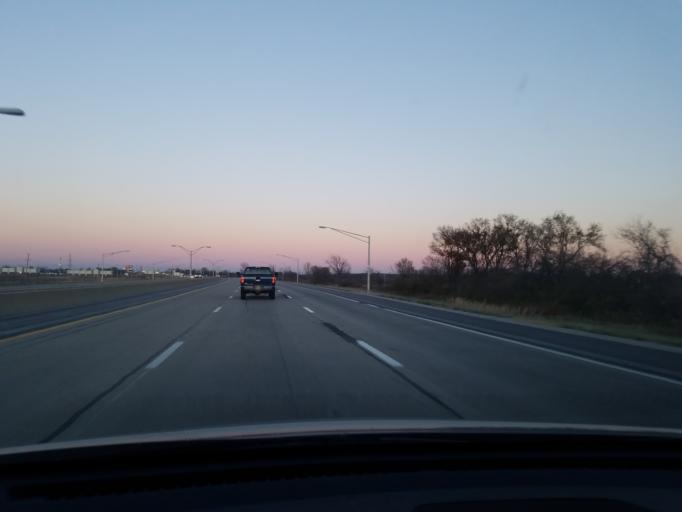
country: US
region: Illinois
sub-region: Saint Clair County
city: Centreville
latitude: 38.5596
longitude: -90.1405
